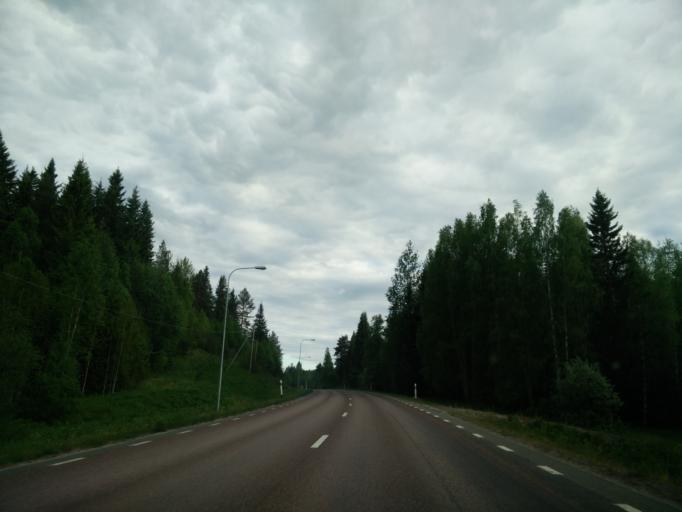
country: SE
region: Jaemtland
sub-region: Harjedalens Kommun
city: Sveg
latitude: 62.2718
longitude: 14.8038
